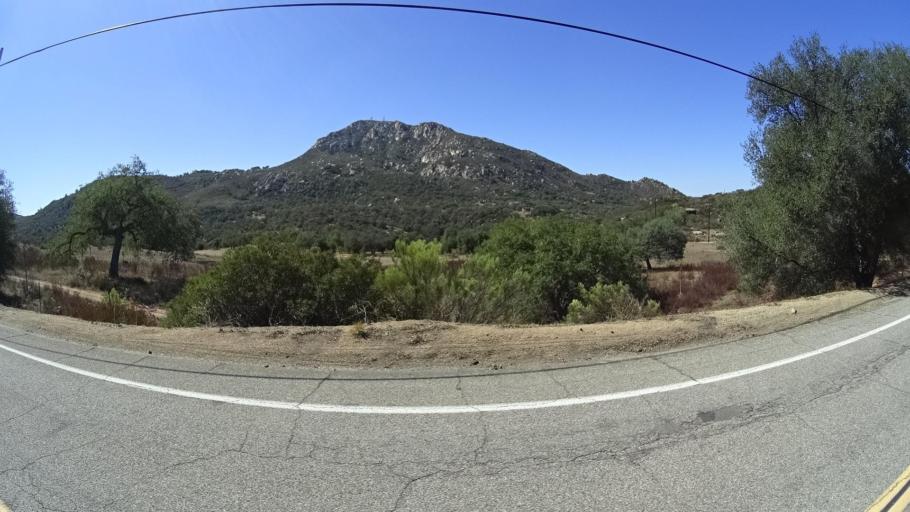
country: US
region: California
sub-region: San Diego County
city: Alpine
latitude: 32.7186
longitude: -116.7557
